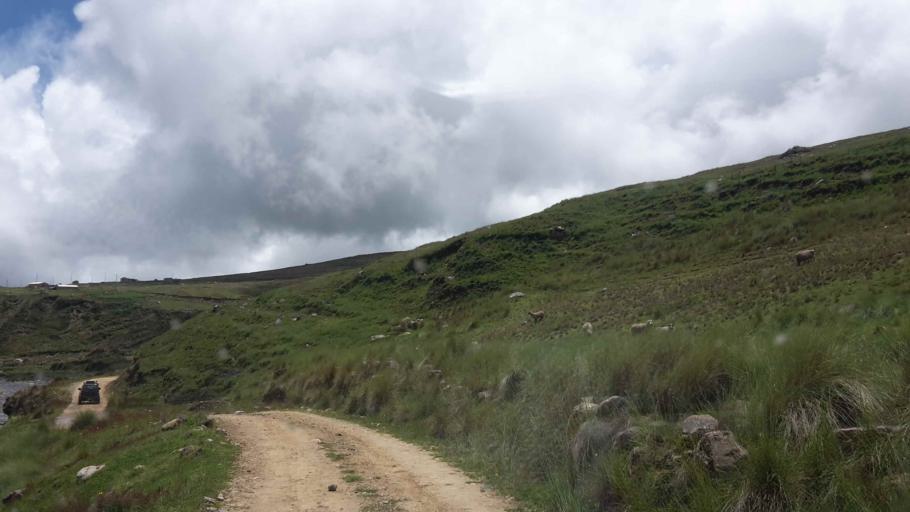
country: BO
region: Cochabamba
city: Cochabamba
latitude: -17.1844
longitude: -66.0651
